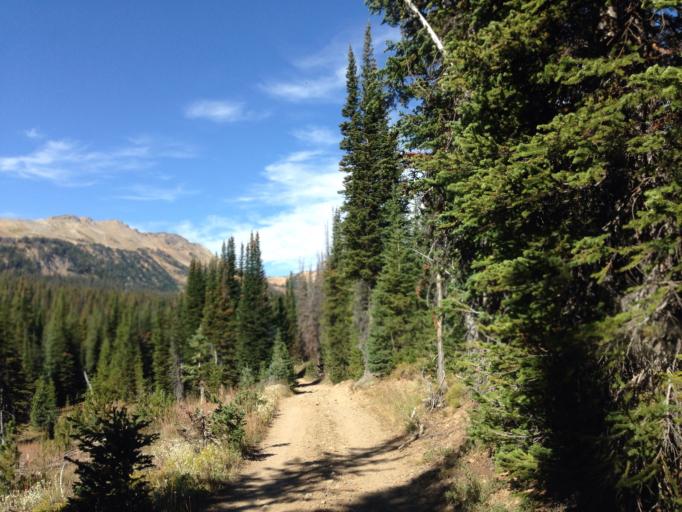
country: US
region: Montana
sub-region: Stillwater County
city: Absarokee
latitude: 45.0510
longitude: -109.9117
